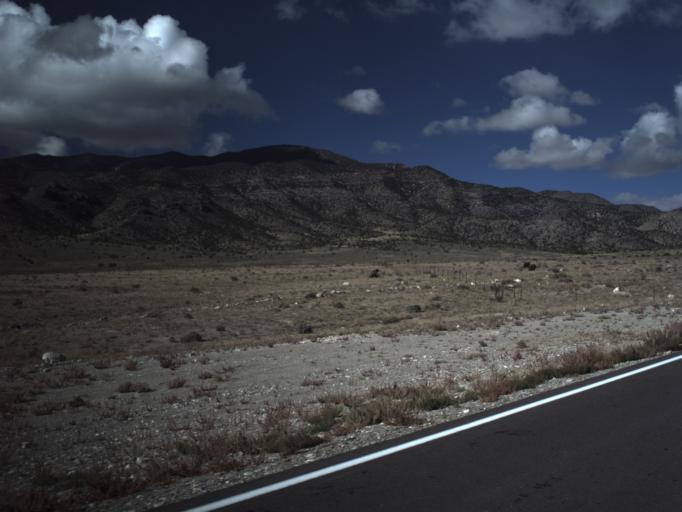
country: US
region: Utah
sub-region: Beaver County
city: Milford
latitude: 38.4966
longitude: -113.4871
